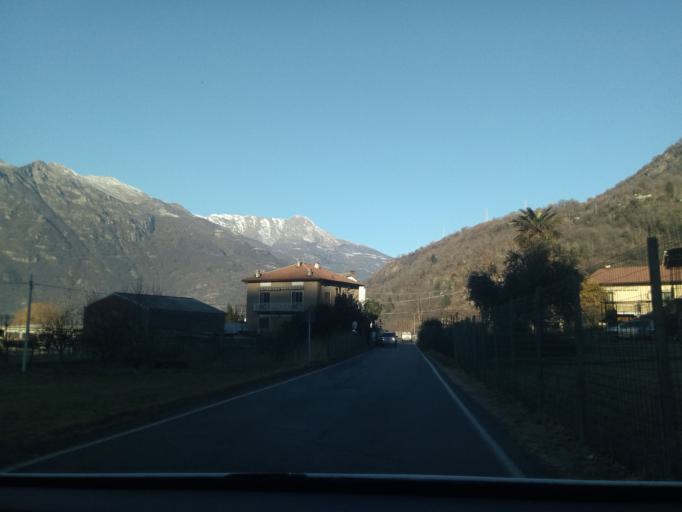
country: IT
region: Piedmont
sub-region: Provincia di Torino
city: Borgofranco d'Ivrea
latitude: 45.5143
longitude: 7.8712
